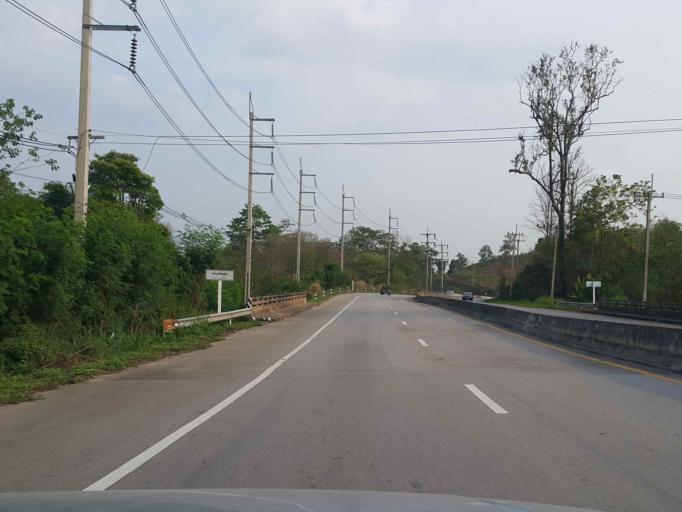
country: TH
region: Chiang Mai
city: Mae Taeng
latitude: 19.2339
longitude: 98.9683
